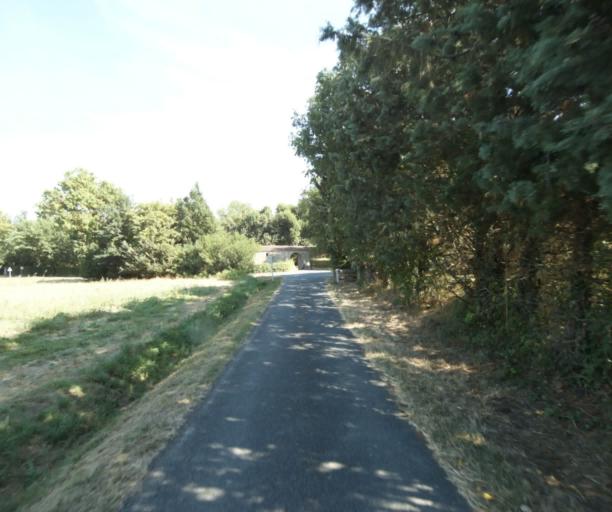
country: FR
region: Midi-Pyrenees
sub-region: Departement de la Haute-Garonne
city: Revel
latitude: 43.5070
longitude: 1.9852
